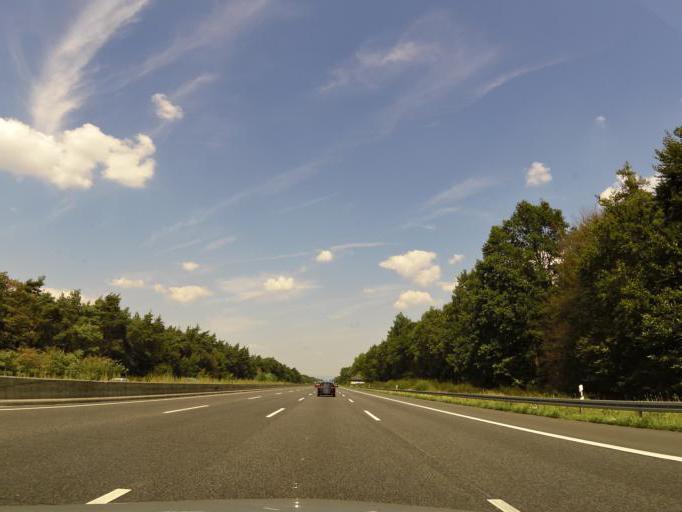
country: DE
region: Hesse
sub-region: Regierungsbezirk Darmstadt
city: Erzhausen
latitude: 49.9605
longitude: 8.6069
